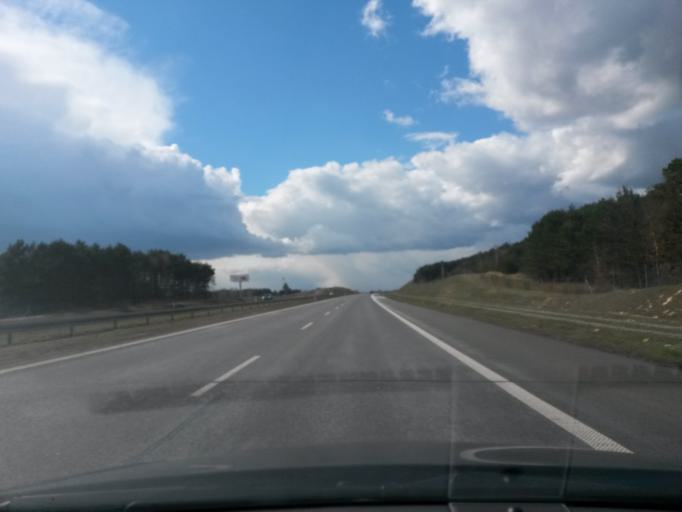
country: PL
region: Greater Poland Voivodeship
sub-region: Powiat kolski
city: Koscielec
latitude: 52.1424
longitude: 18.5304
